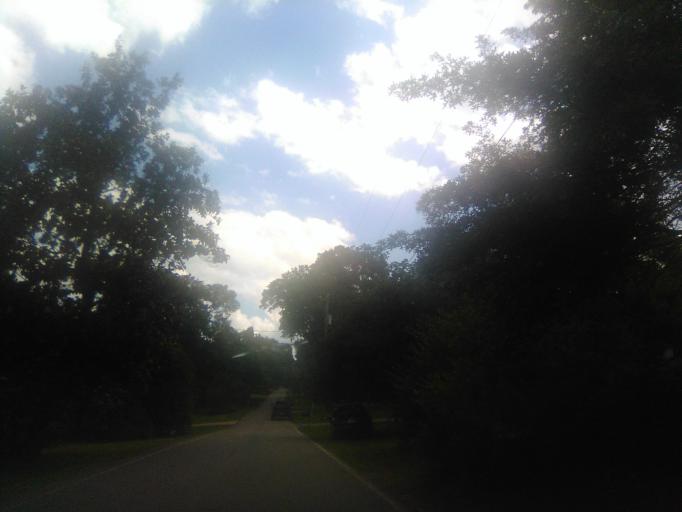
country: US
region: Tennessee
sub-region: Davidson County
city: Belle Meade
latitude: 36.1140
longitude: -86.8441
